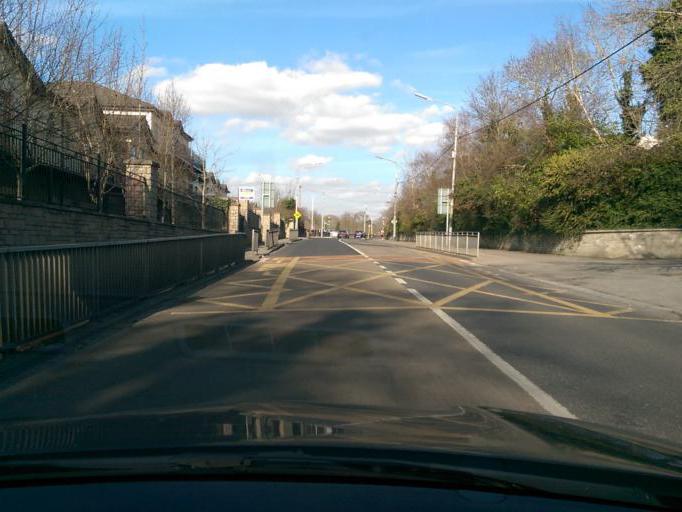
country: IE
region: Leinster
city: Lucan
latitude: 53.3586
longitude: -6.4410
